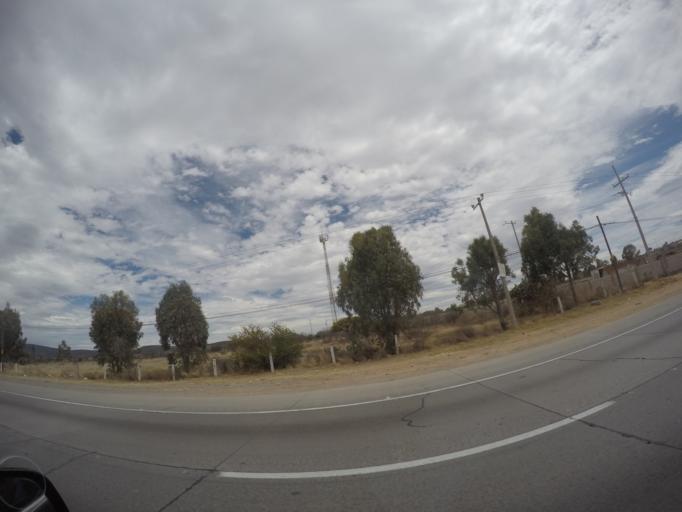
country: MX
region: Queretaro
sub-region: San Juan del Rio
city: Paso de Mata
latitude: 20.3080
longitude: -99.9342
